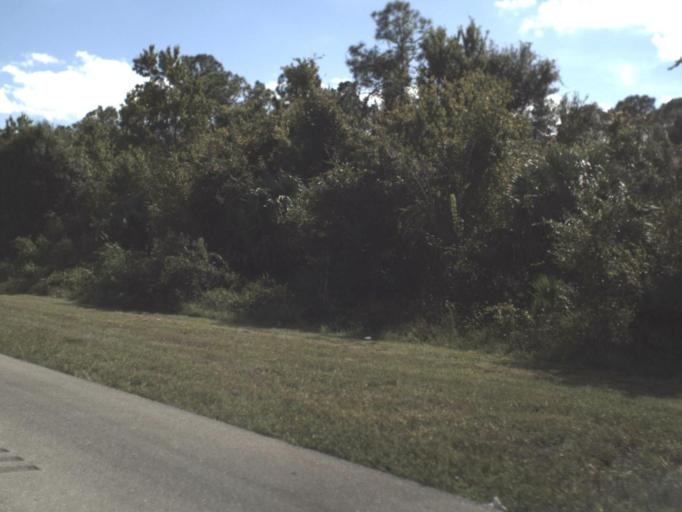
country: US
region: Florida
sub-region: Indian River County
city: Fellsmere
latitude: 27.5757
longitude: -80.8037
